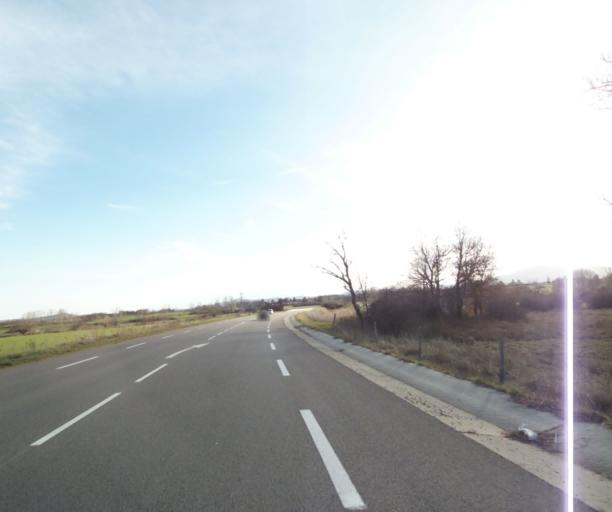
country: FR
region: Rhone-Alpes
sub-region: Departement de l'Ardeche
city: Davezieux
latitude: 45.2501
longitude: 4.7169
